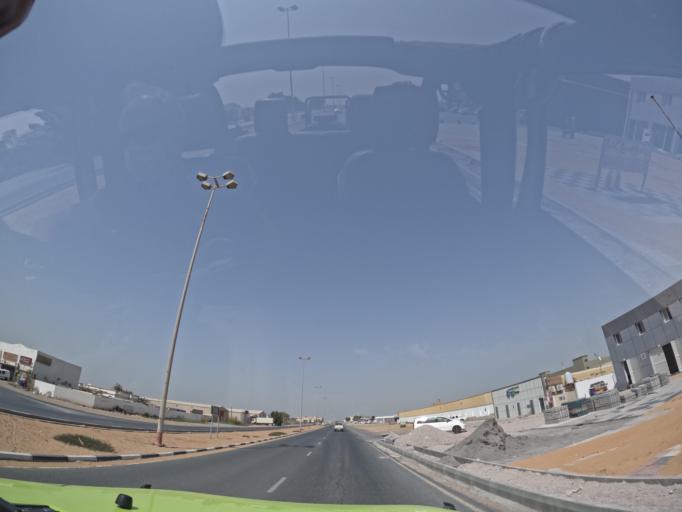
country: AE
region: Umm al Qaywayn
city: Umm al Qaywayn
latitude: 25.5033
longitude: 55.5613
